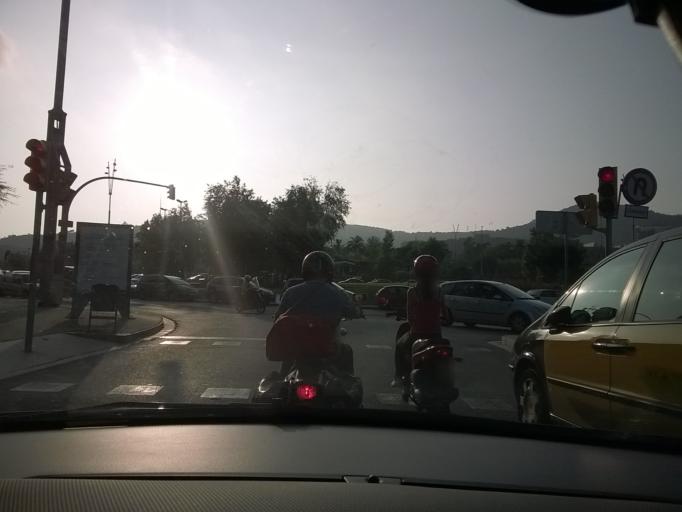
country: ES
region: Catalonia
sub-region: Provincia de Barcelona
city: Horta-Guinardo
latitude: 41.4261
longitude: 2.1508
